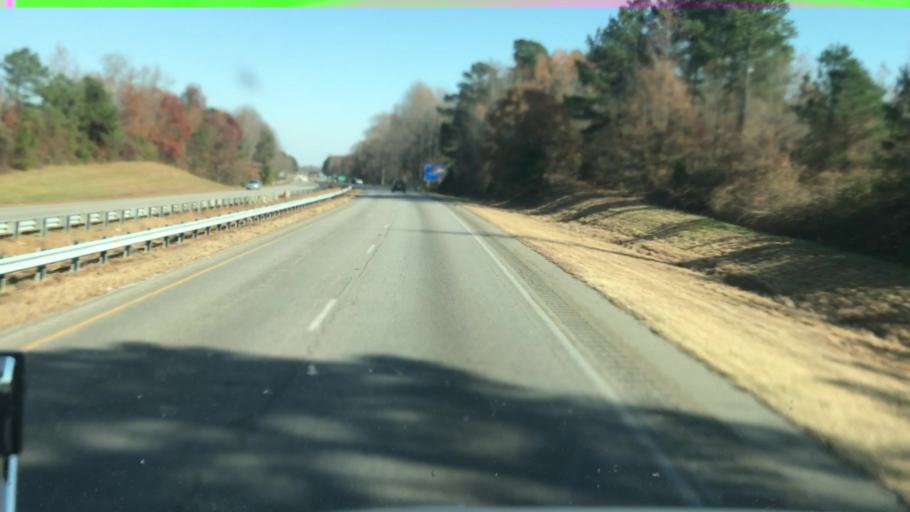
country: US
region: North Carolina
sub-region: Nash County
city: Nashville
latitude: 35.9770
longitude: -77.9117
